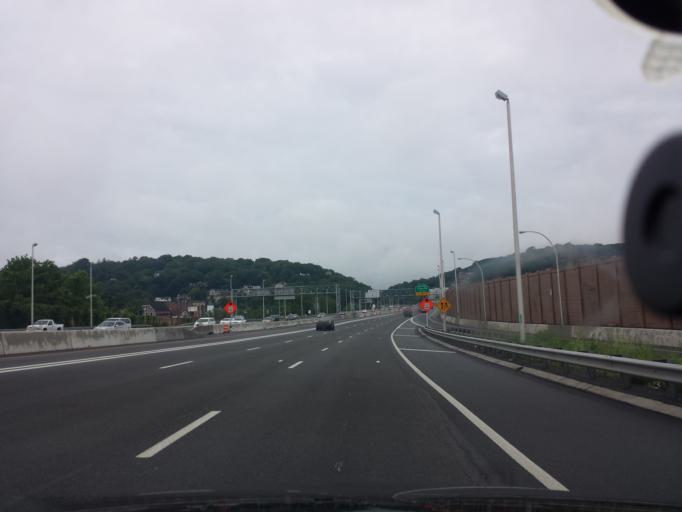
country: US
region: New Jersey
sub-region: Hudson County
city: Bayonne
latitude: 40.6071
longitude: -74.0850
